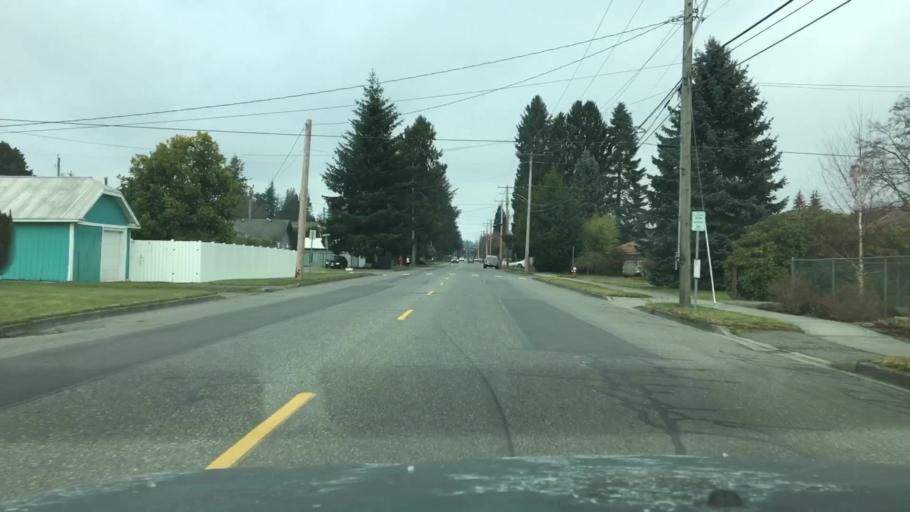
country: US
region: Washington
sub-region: Skagit County
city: Sedro-Woolley
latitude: 48.5000
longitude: -122.2259
